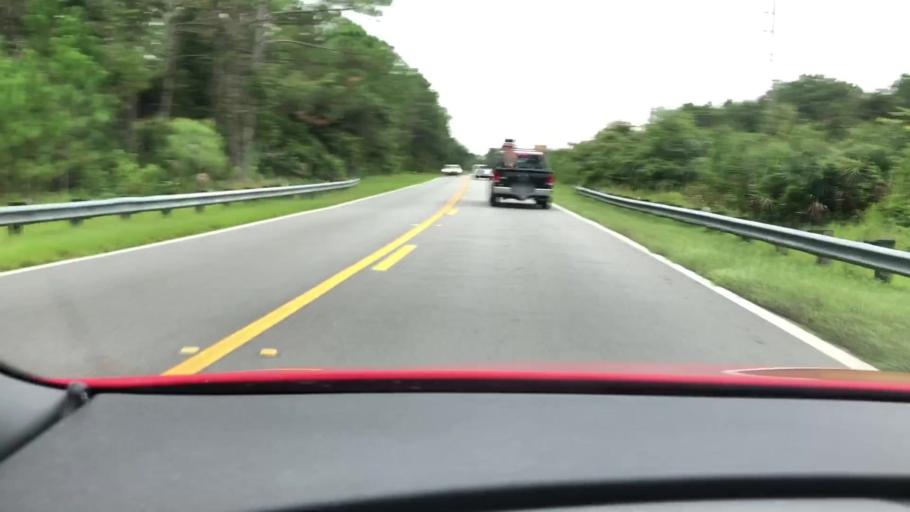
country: US
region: Florida
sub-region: Flagler County
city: Palm Coast
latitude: 29.5159
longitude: -81.1968
